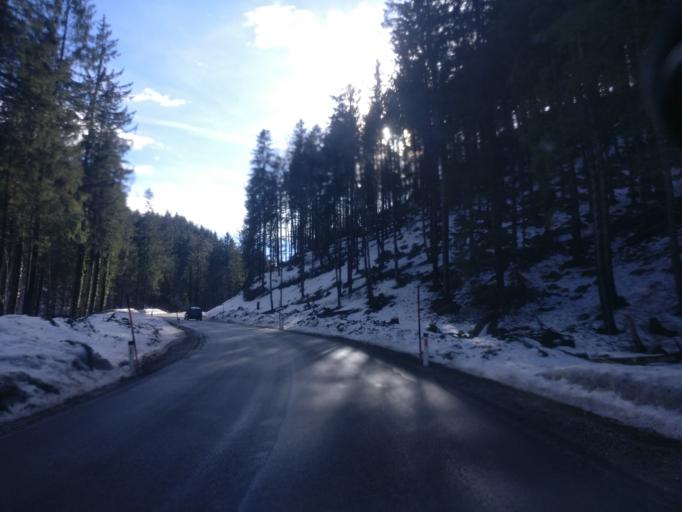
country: AT
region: Styria
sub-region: Politischer Bezirk Liezen
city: Sankt Gallen
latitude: 47.6414
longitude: 14.5683
